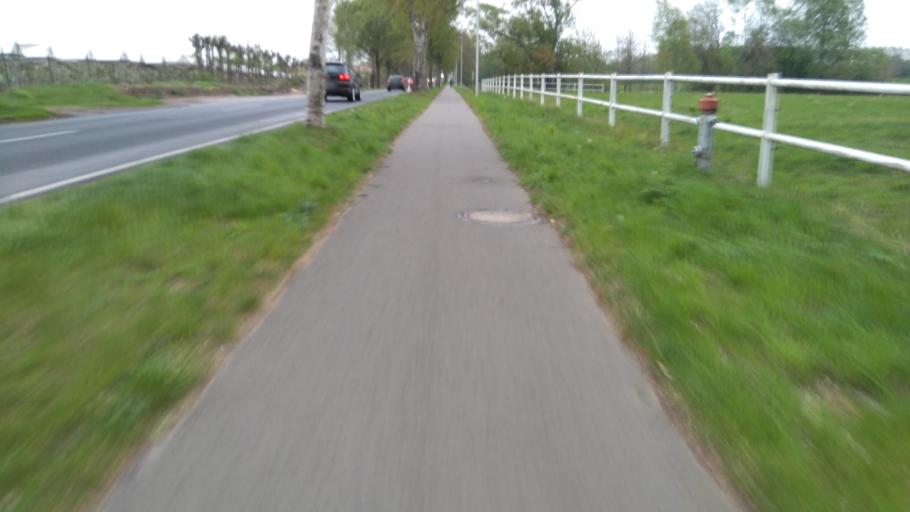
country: DE
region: Lower Saxony
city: Apensen
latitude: 53.4492
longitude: 9.6417
